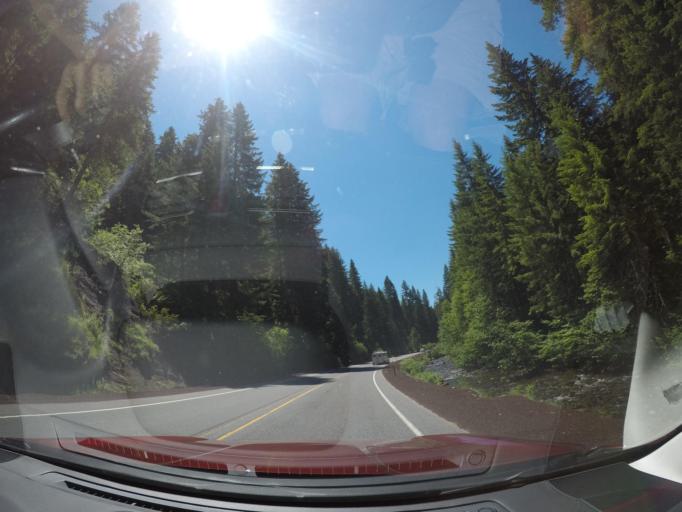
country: US
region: Oregon
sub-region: Deschutes County
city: Sisters
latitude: 44.5465
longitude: -121.9941
